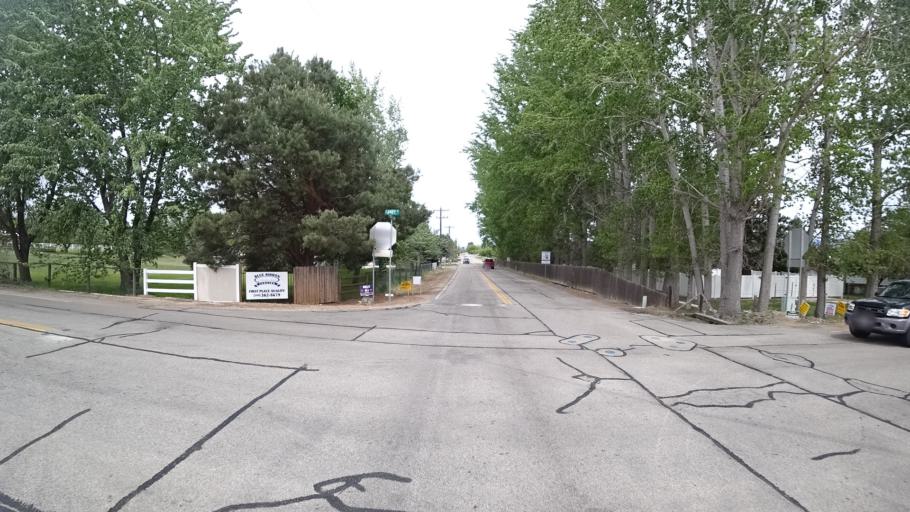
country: US
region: Idaho
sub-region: Ada County
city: Meridian
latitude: 43.5612
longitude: -116.3744
